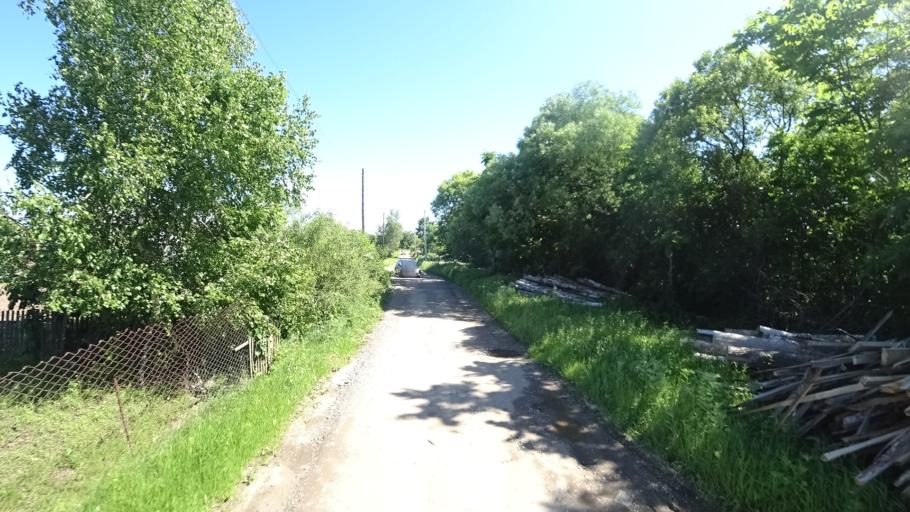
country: RU
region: Khabarovsk Krai
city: Khor
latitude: 47.8863
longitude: 135.0263
